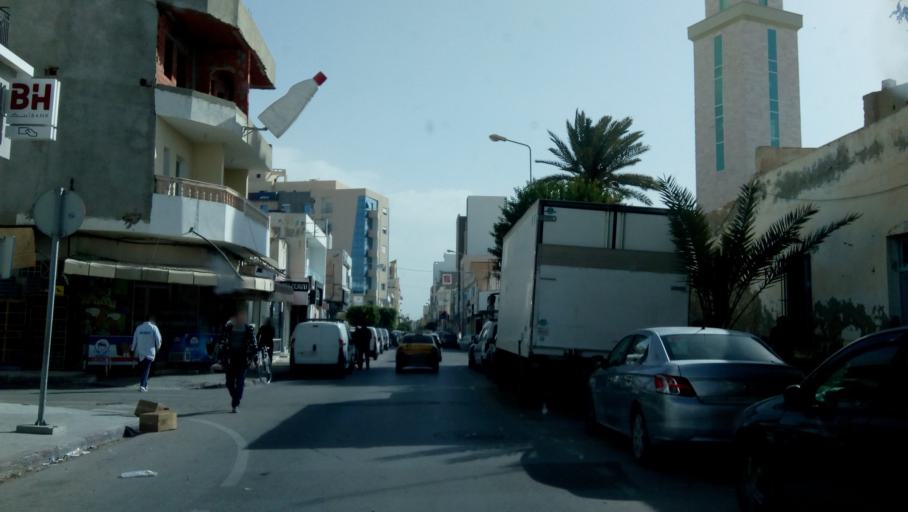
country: TN
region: Qabis
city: Gabes
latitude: 33.8860
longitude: 10.1013
